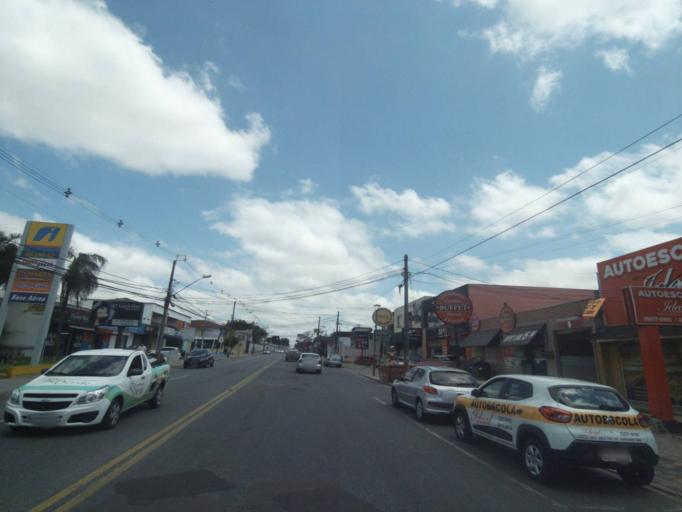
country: BR
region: Parana
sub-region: Curitiba
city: Curitiba
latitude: -25.3967
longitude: -49.2329
